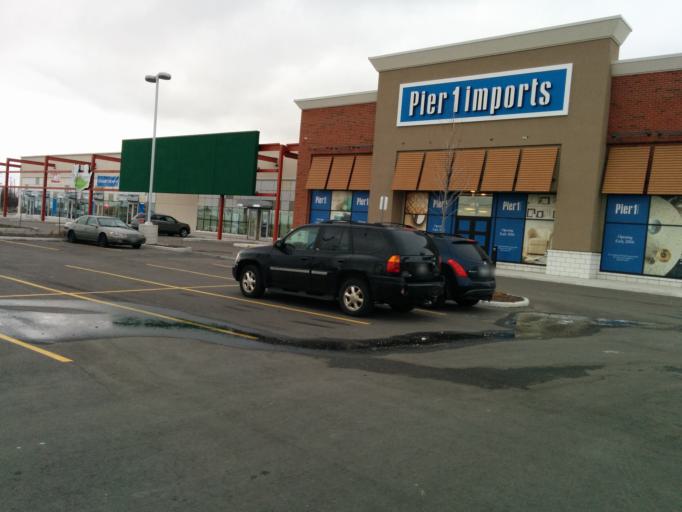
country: CA
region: Ontario
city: Etobicoke
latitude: 43.6188
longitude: -79.5583
